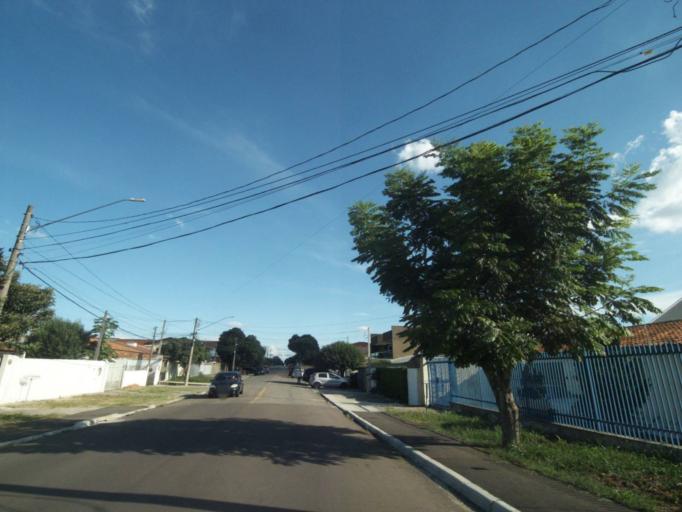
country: BR
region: Parana
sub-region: Pinhais
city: Pinhais
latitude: -25.4453
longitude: -49.2124
